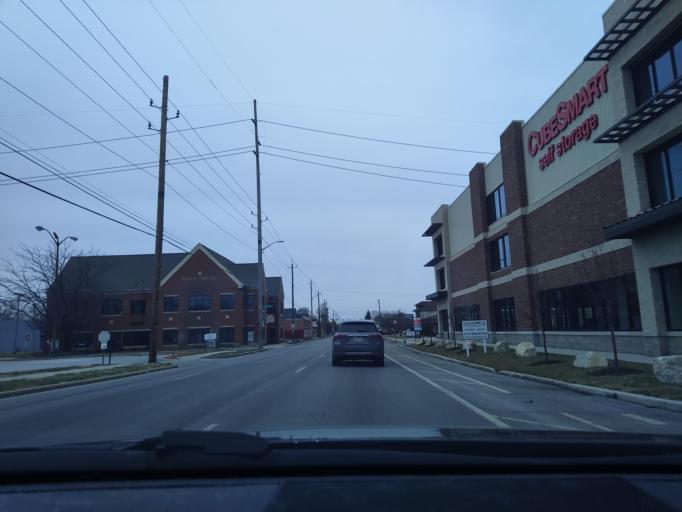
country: US
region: Indiana
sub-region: Marion County
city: Indianapolis
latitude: 39.7956
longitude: -86.1591
